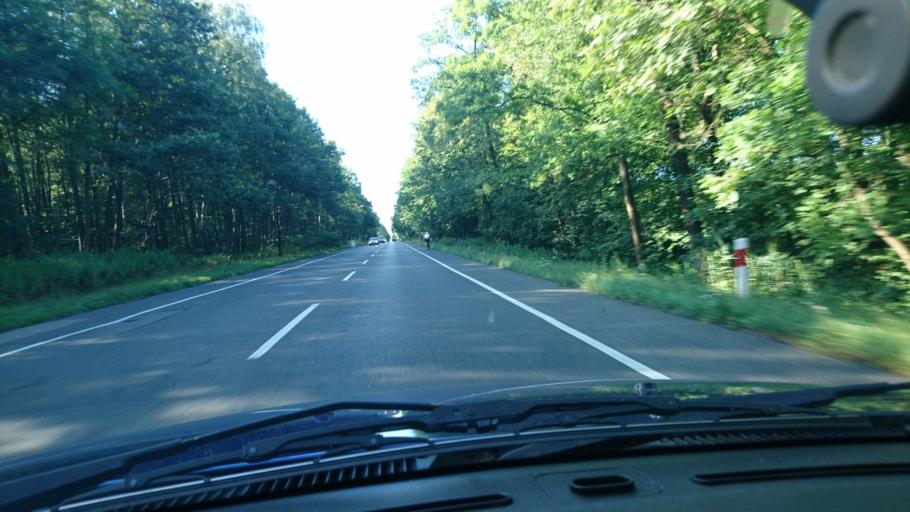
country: PL
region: Silesian Voivodeship
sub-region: Gliwice
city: Gliwice
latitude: 50.3346
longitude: 18.6560
